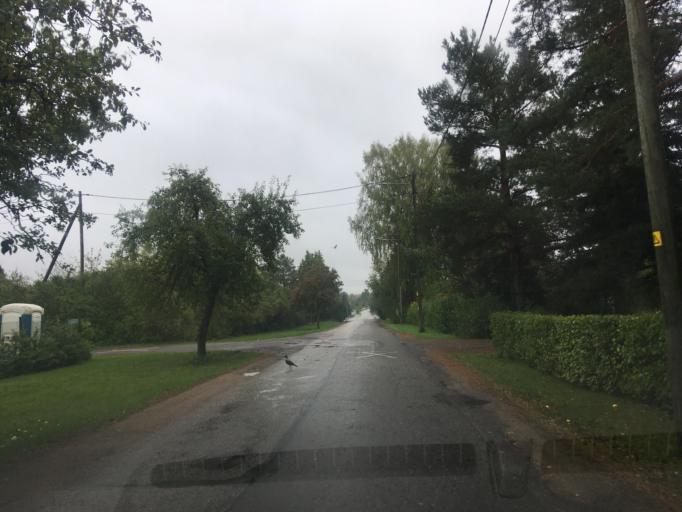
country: EE
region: Tartu
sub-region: UElenurme vald
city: Ulenurme
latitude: 58.3456
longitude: 26.7838
